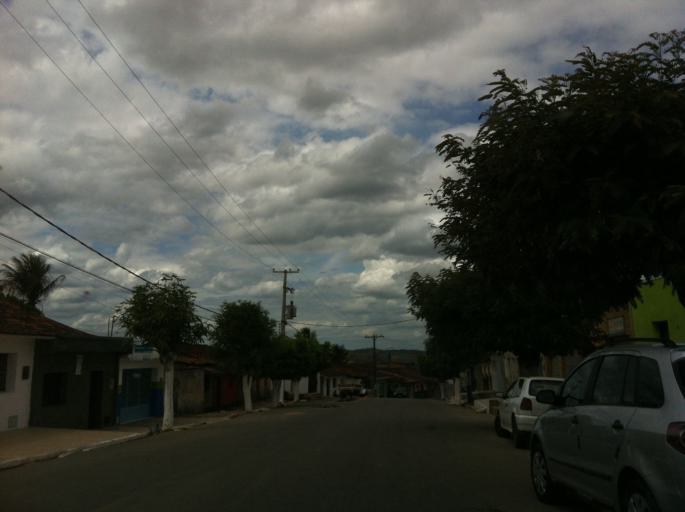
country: BR
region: Alagoas
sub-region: Ibateguara
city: Ibateguara
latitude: -8.9689
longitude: -35.9250
